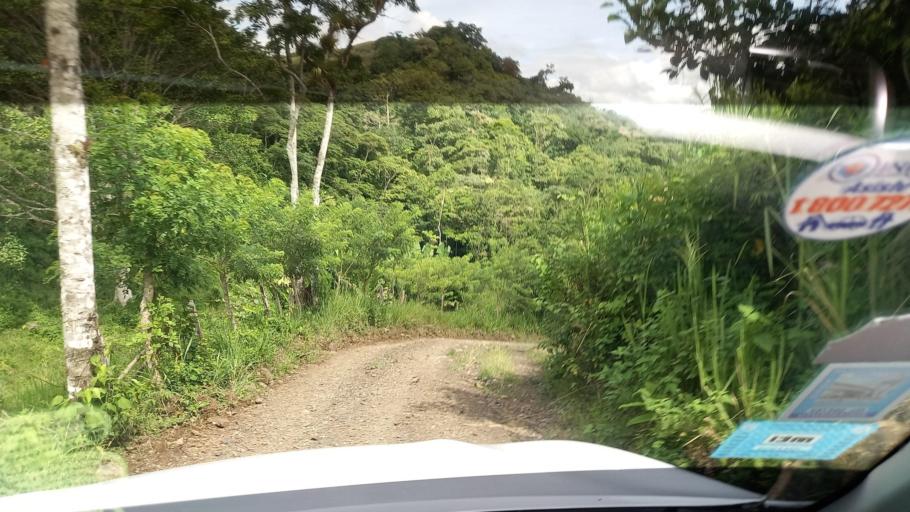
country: NI
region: Jinotega
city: San Jose de Bocay
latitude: 13.3962
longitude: -85.6967
